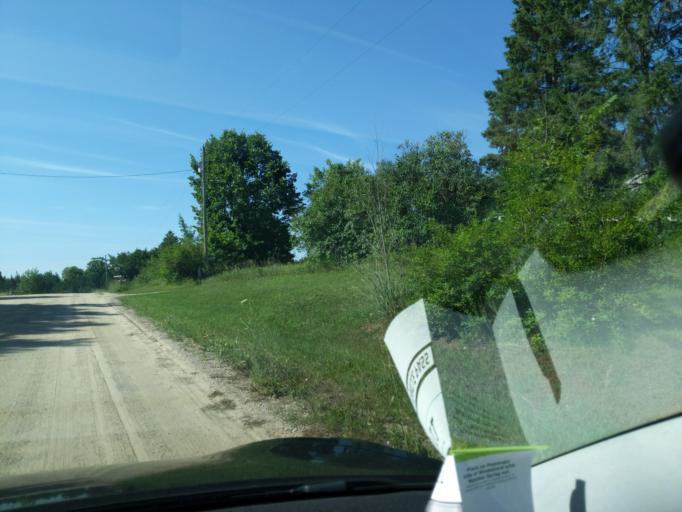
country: US
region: Michigan
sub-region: Cheboygan County
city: Cheboygan
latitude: 45.6688
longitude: -84.6509
